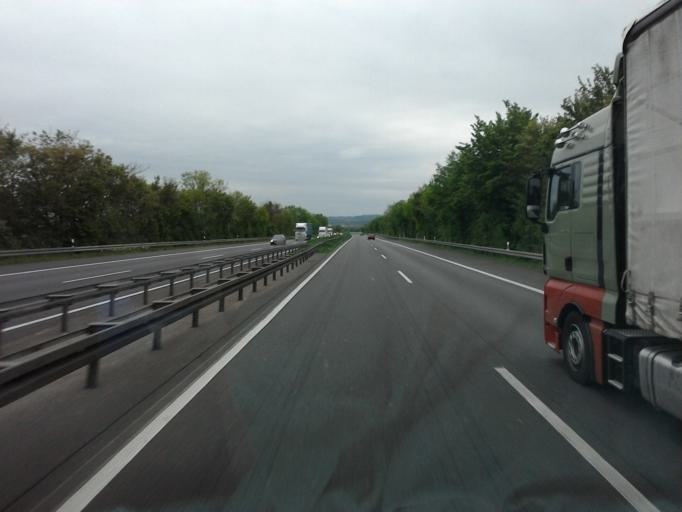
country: DE
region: North Rhine-Westphalia
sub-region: Regierungsbezirk Koln
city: Rheinbach
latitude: 50.6654
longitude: 6.9227
